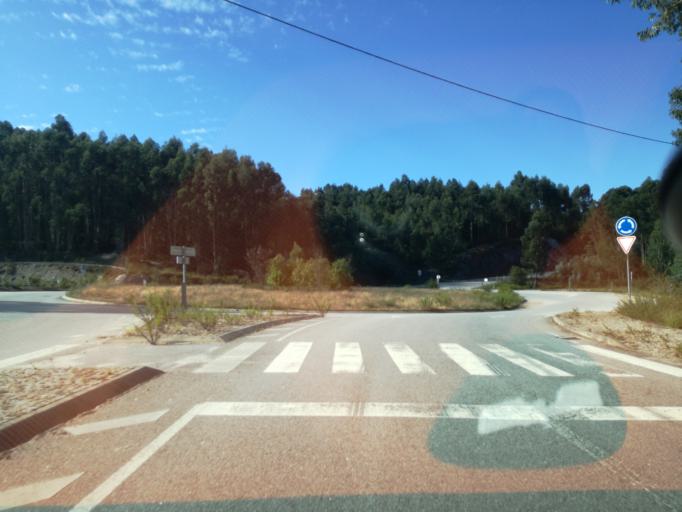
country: PT
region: Porto
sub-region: Pacos de Ferreira
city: Seroa
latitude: 41.2831
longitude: -8.4246
